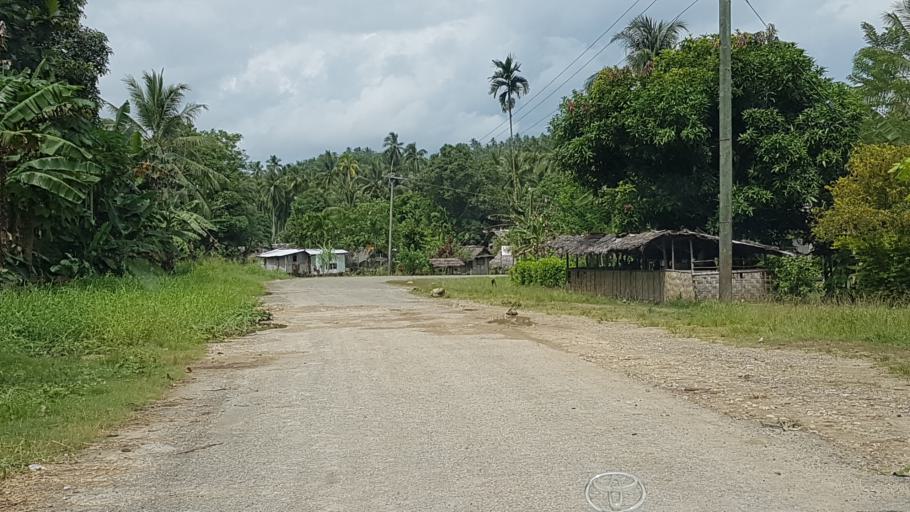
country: PG
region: Madang
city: Madang
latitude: -4.7919
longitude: 145.7175
